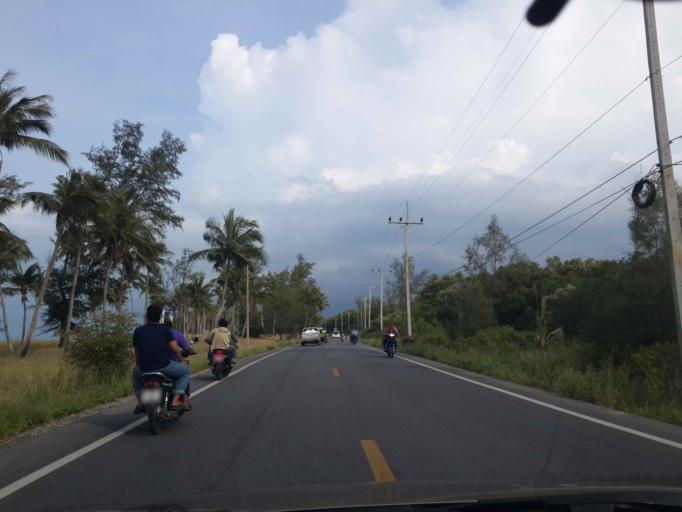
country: TH
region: Pattani
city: Yaring
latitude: 6.9074
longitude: 101.3494
